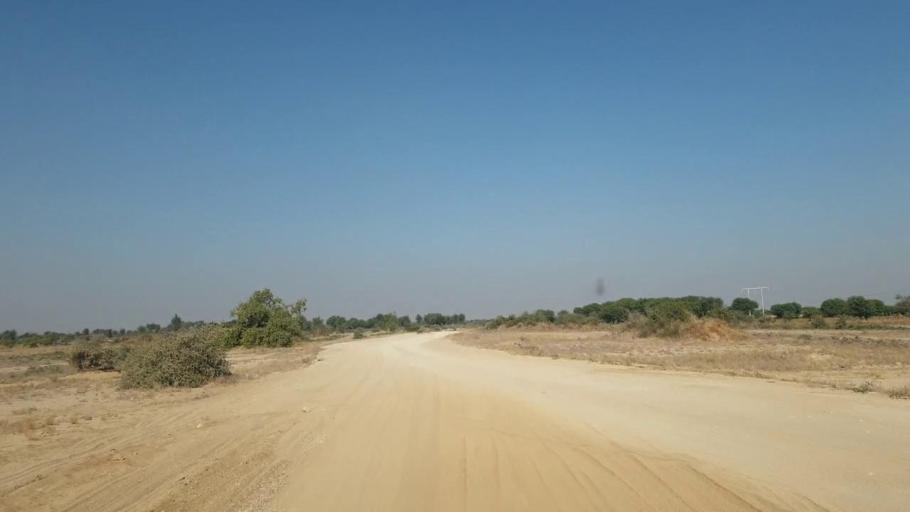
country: PK
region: Sindh
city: Jamshoro
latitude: 25.2982
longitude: 67.8151
